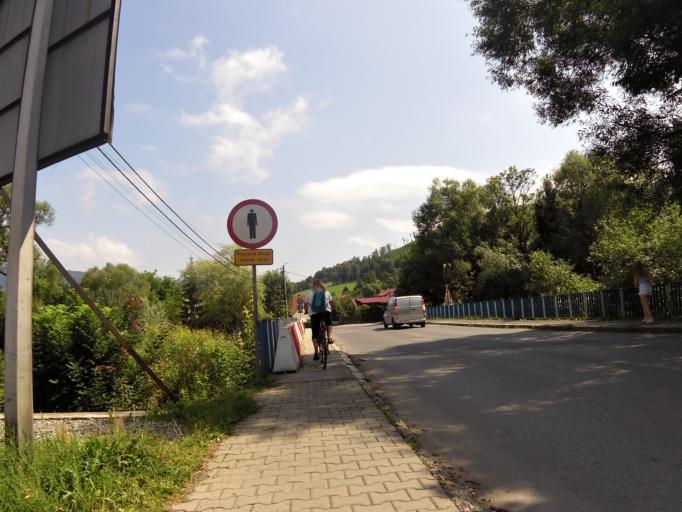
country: PL
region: Silesian Voivodeship
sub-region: Powiat zywiecki
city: Rajcza
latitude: 49.5017
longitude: 19.0973
